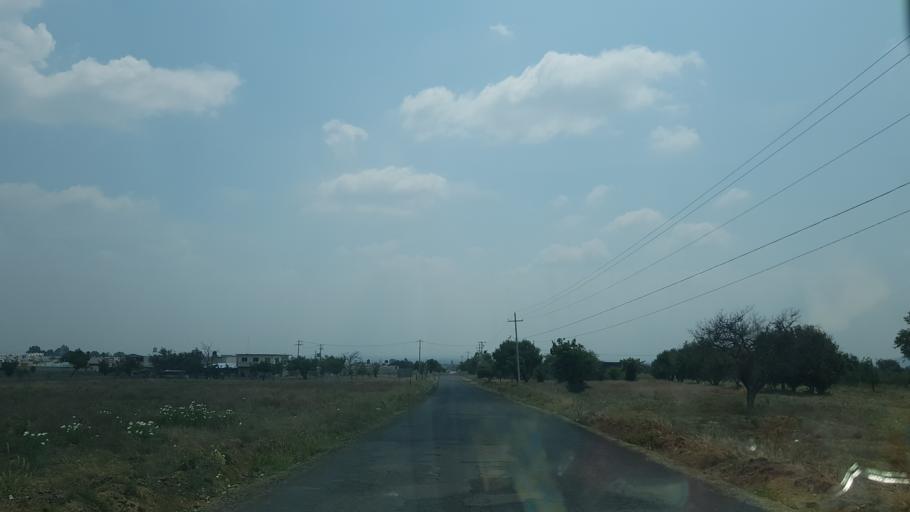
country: MX
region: Puebla
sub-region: Huejotzingo
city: San Juan Pancoac
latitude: 19.1374
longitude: -98.4226
